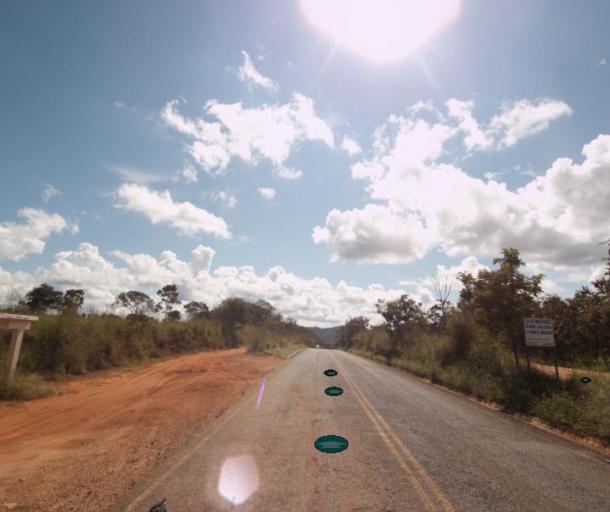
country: BR
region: Goias
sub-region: Pirenopolis
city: Pirenopolis
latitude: -15.7825
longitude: -49.0445
